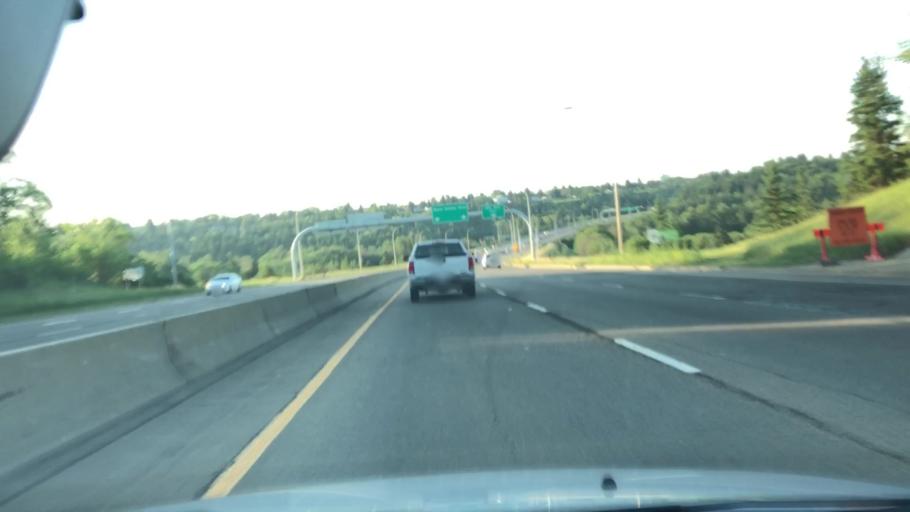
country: CA
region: Alberta
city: Edmonton
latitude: 53.5603
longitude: -113.4430
